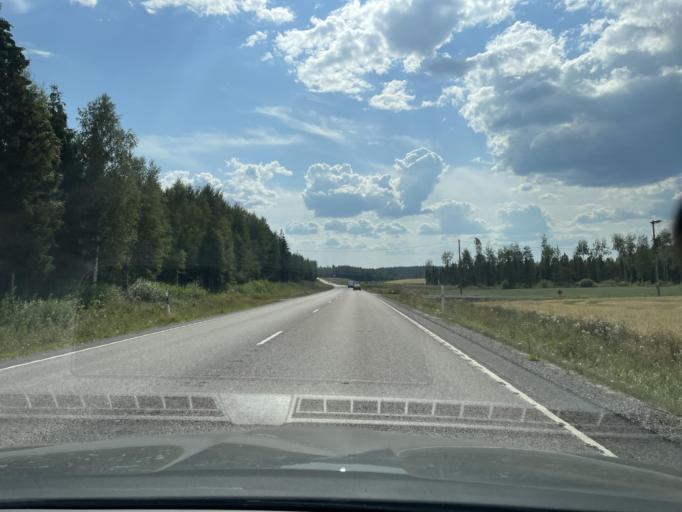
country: FI
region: Central Finland
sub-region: Jyvaeskylae
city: Korpilahti
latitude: 61.9641
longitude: 25.3764
